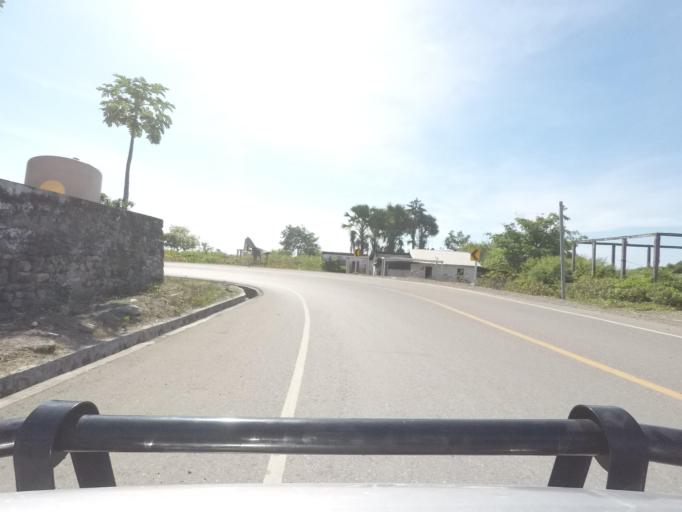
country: ID
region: East Nusa Tenggara
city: Atambua
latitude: -8.9461
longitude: 124.9729
